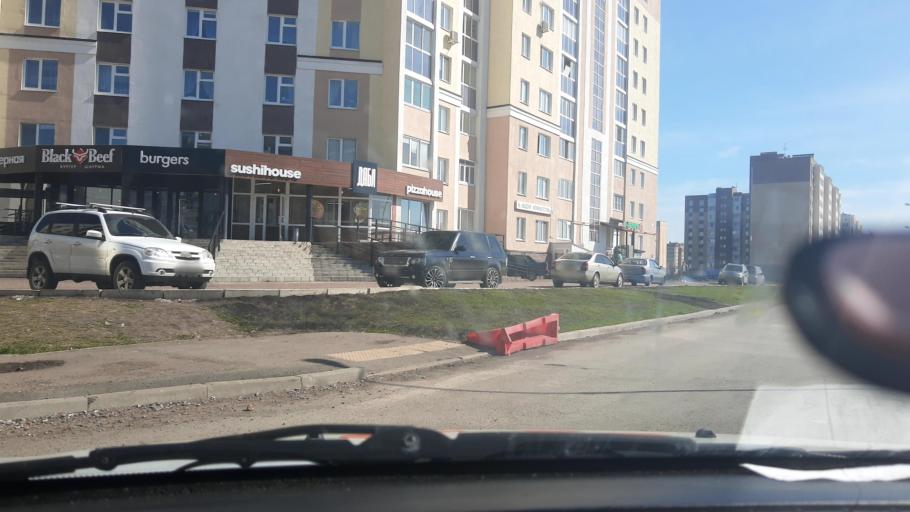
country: RU
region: Bashkortostan
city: Sterlitamak
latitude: 53.6263
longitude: 55.8963
